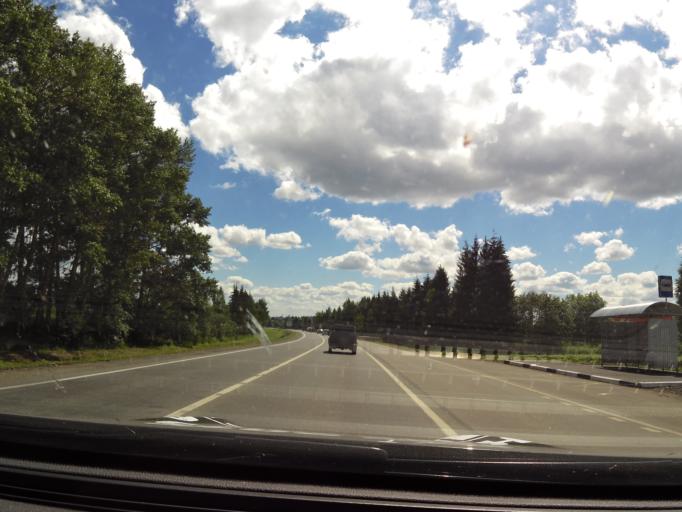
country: RU
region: Vologda
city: Molochnoye
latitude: 59.2891
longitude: 39.6910
